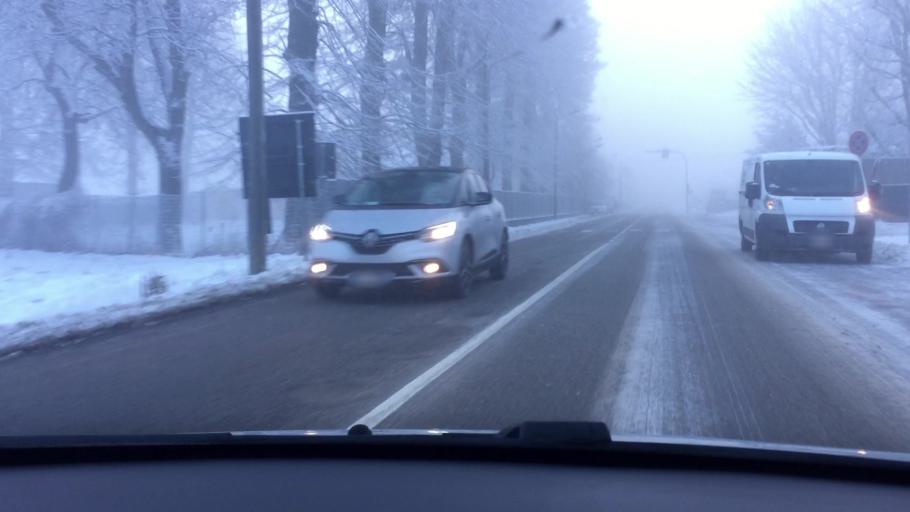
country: IT
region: Piedmont
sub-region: Provincia di Torino
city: Scalenghe
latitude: 44.8926
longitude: 7.4921
